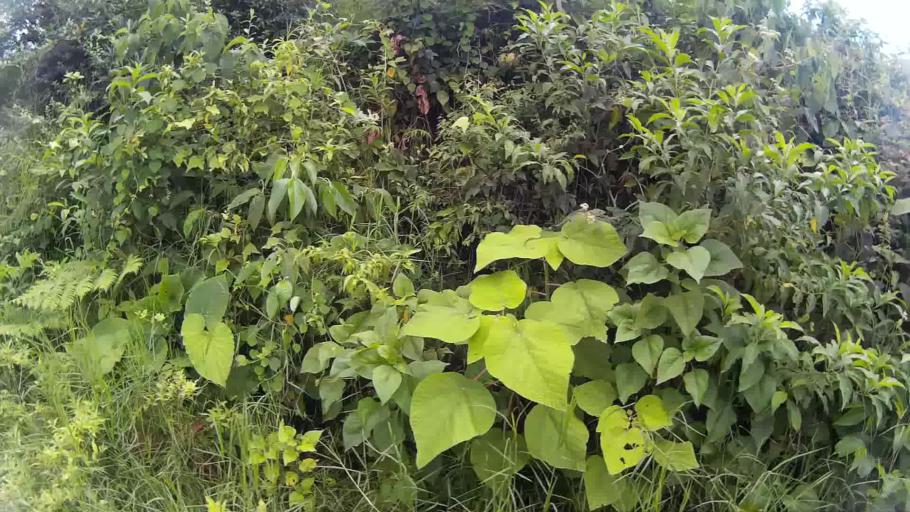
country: CO
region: Valle del Cauca
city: Ulloa
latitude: 4.7203
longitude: -75.7161
